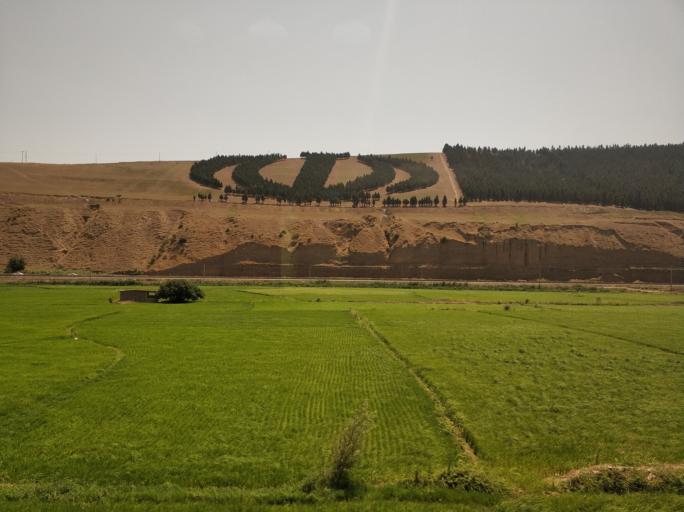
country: IR
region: Gilan
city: Pa'in-e Bazar-e Rudbar
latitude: 36.9148
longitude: 49.5208
